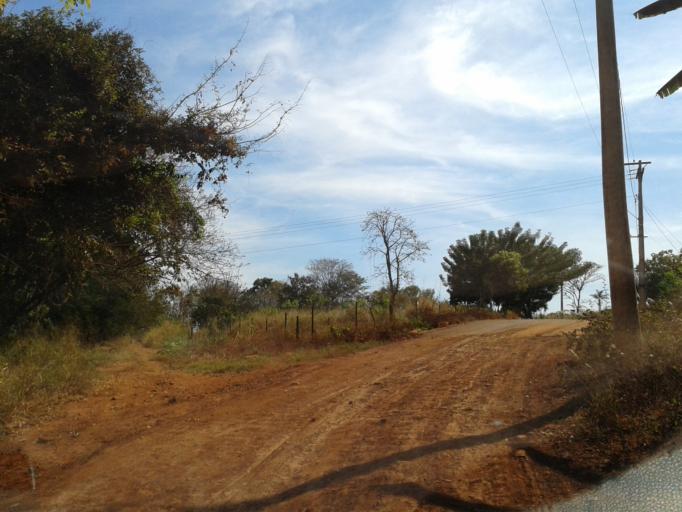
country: BR
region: Minas Gerais
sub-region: Ituiutaba
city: Ituiutaba
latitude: -18.9580
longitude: -49.4656
